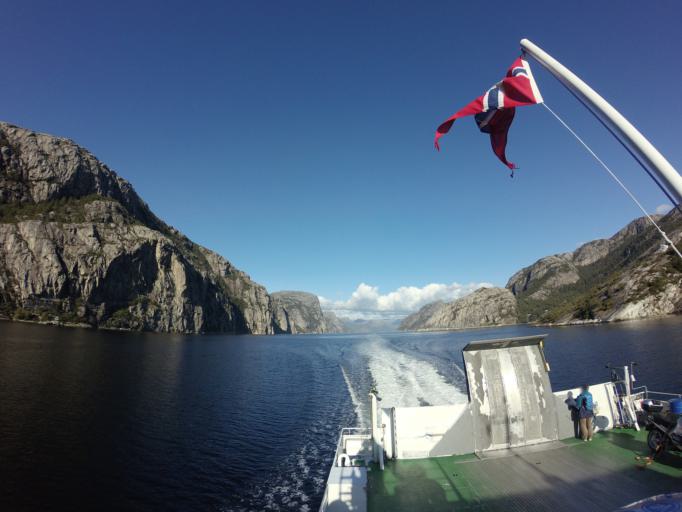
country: NO
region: Rogaland
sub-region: Forsand
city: Forsand
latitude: 58.9494
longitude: 6.1294
